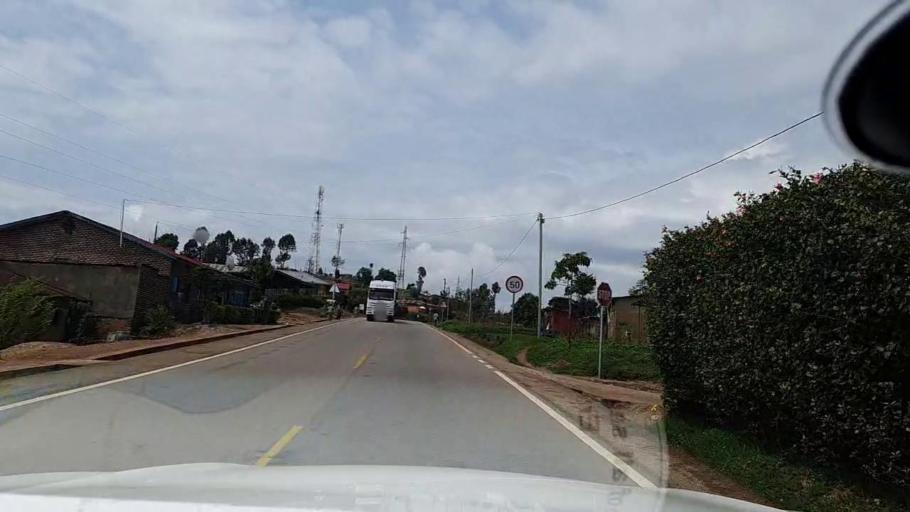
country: RW
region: Southern Province
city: Nzega
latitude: -2.4835
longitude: 29.5326
